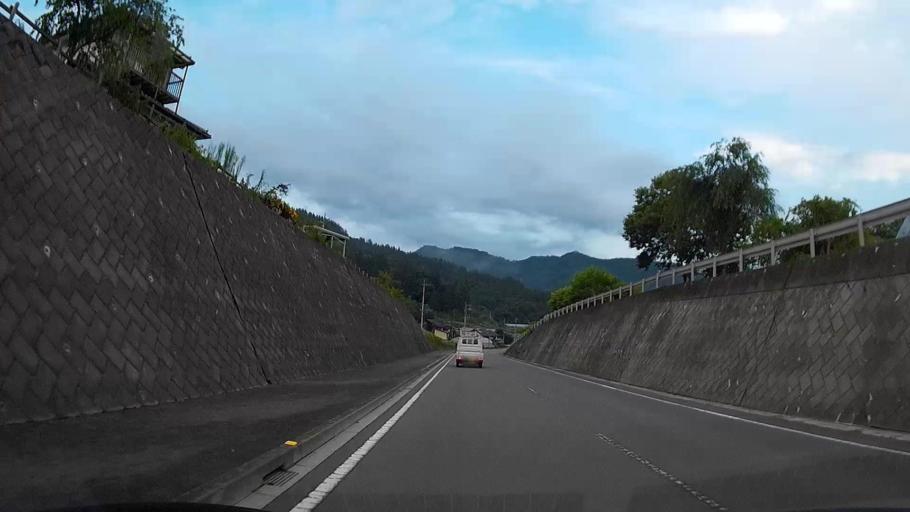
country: JP
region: Gunma
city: Nakanojomachi
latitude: 36.5249
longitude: 138.7502
